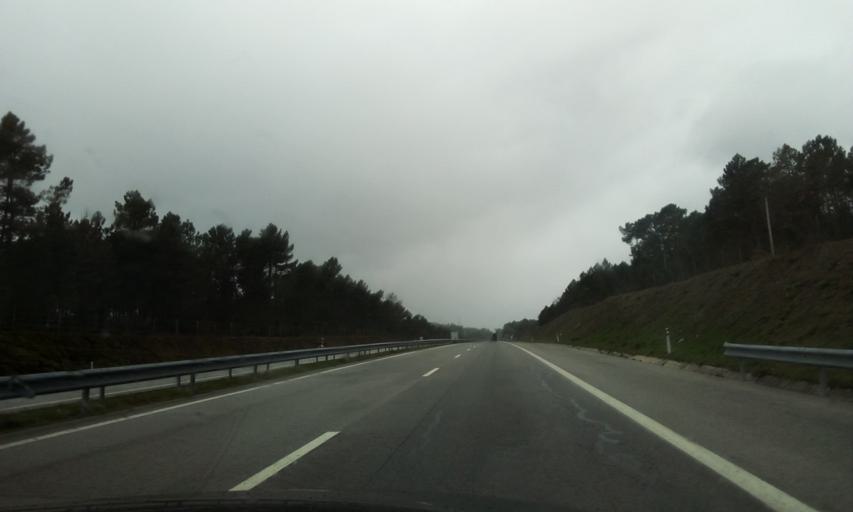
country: PT
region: Guarda
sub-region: Fornos de Algodres
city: Fornos de Algodres
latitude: 40.6144
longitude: -7.6313
